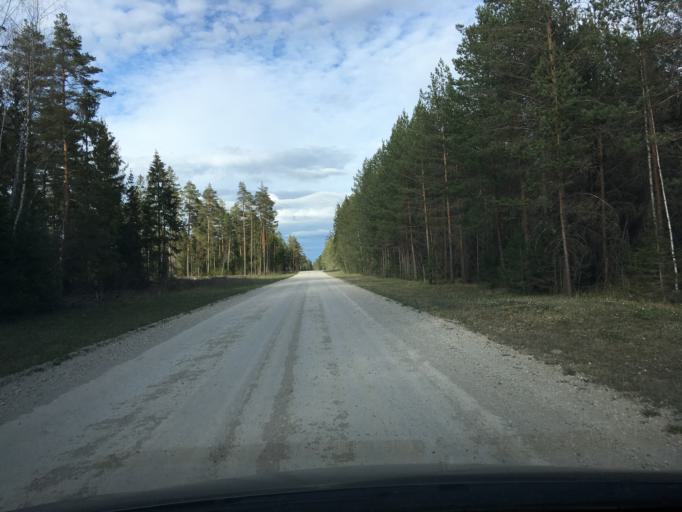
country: EE
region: Raplamaa
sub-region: Maerjamaa vald
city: Marjamaa
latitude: 59.0138
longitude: 24.4126
